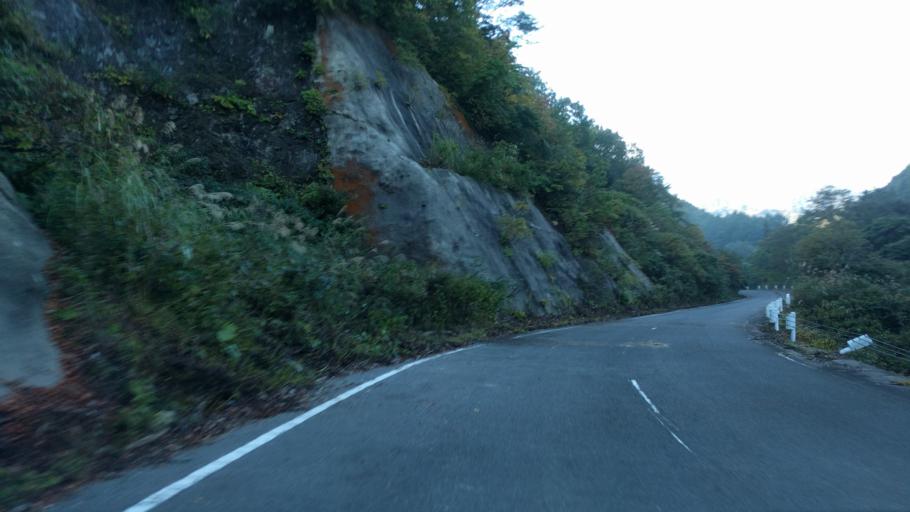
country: JP
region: Fukushima
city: Kitakata
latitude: 37.3972
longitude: 139.7589
